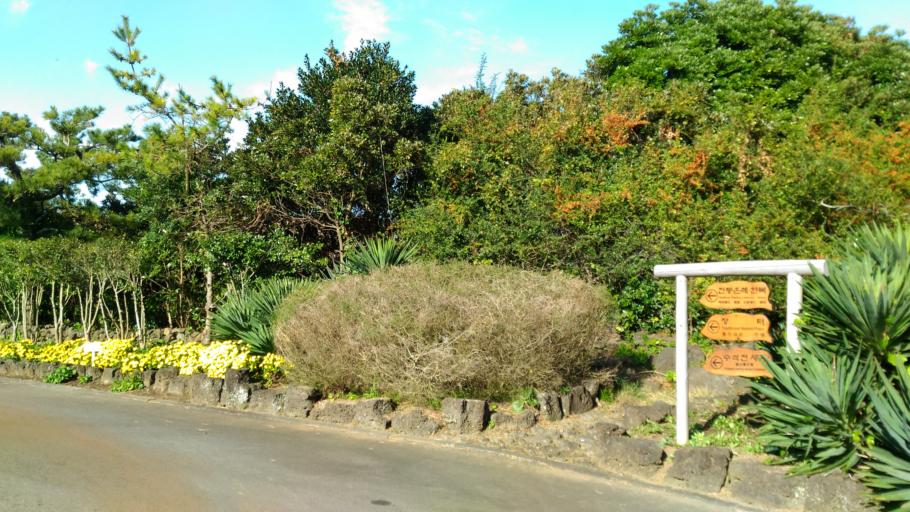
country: KR
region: Jeju-do
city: Seogwipo
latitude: 33.3207
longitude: 126.8434
